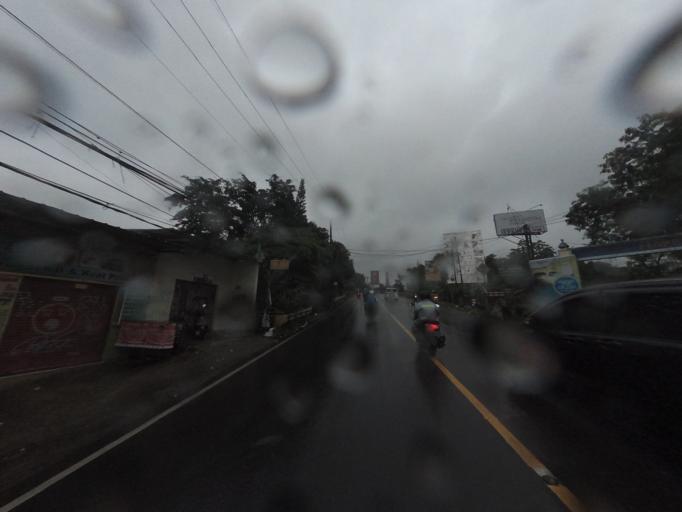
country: ID
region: West Java
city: Caringin
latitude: -6.6526
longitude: 106.8705
